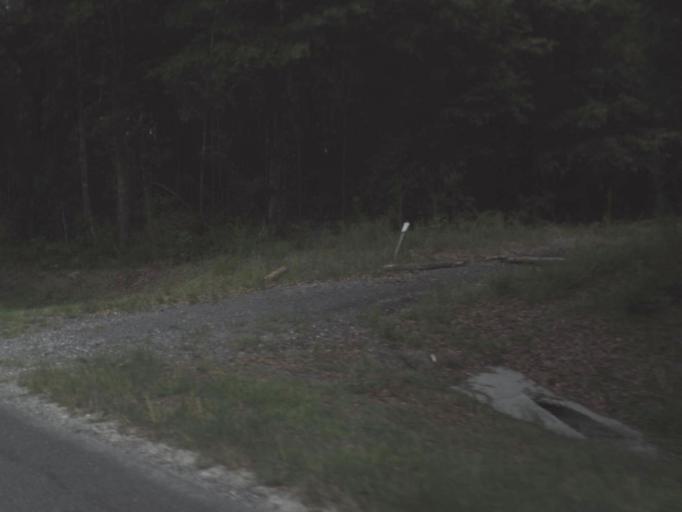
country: US
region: Florida
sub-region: Suwannee County
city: Wellborn
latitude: 30.0818
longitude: -82.7665
